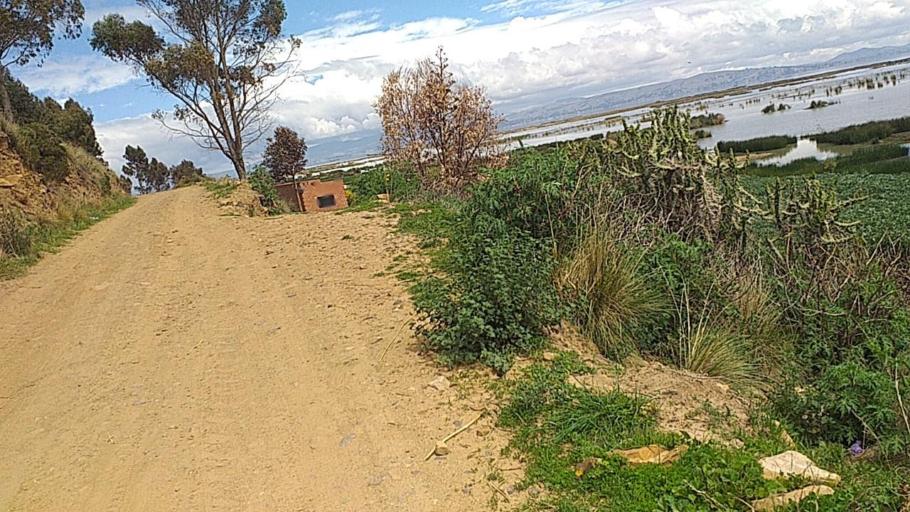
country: BO
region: La Paz
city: Batallas
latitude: -16.3267
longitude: -68.6434
